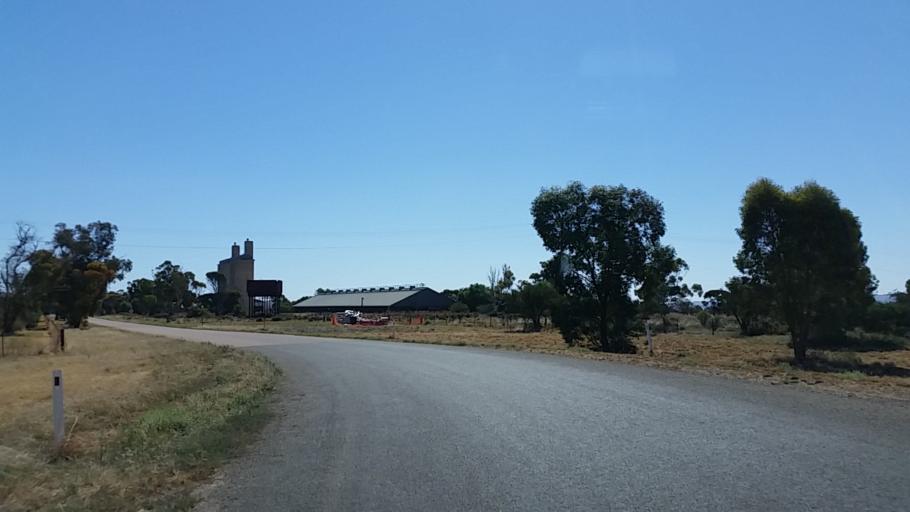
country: AU
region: South Australia
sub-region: Peterborough
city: Peterborough
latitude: -32.7334
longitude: 138.6216
